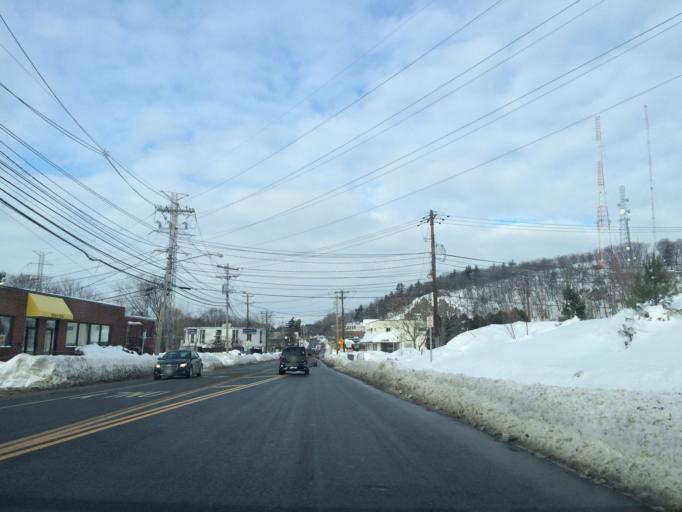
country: US
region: Massachusetts
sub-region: Middlesex County
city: Waltham
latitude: 42.3766
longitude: -71.2633
